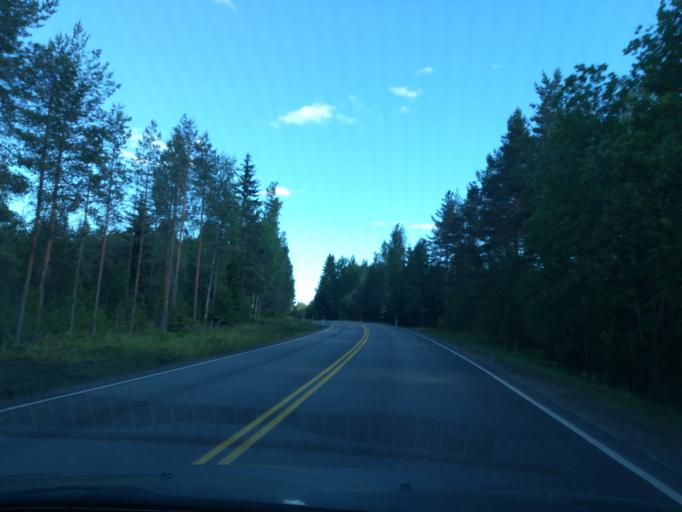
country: FI
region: South Karelia
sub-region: Imatra
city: Ruokolahti
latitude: 61.3753
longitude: 28.6584
